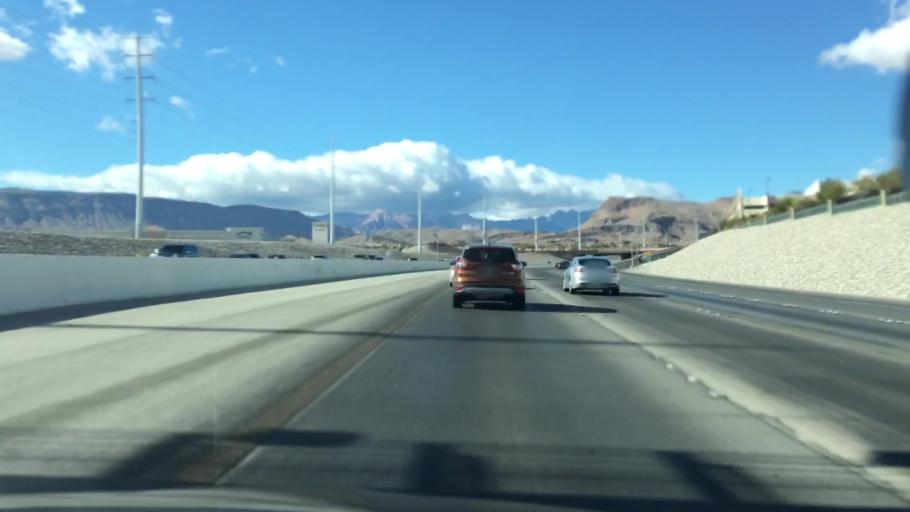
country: US
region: Nevada
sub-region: Clark County
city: Summerlin South
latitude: 36.1197
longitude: -115.3200
